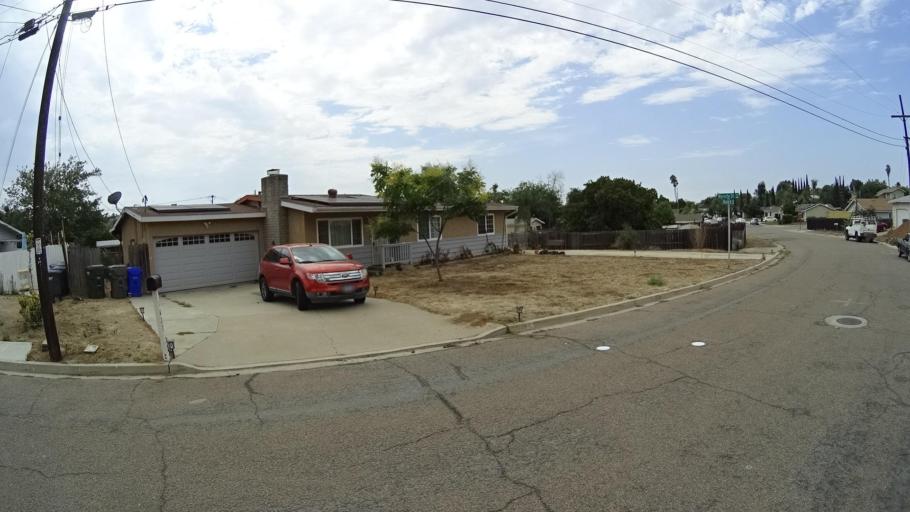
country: US
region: California
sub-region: San Diego County
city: Escondido
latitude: 33.1479
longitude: -117.1211
